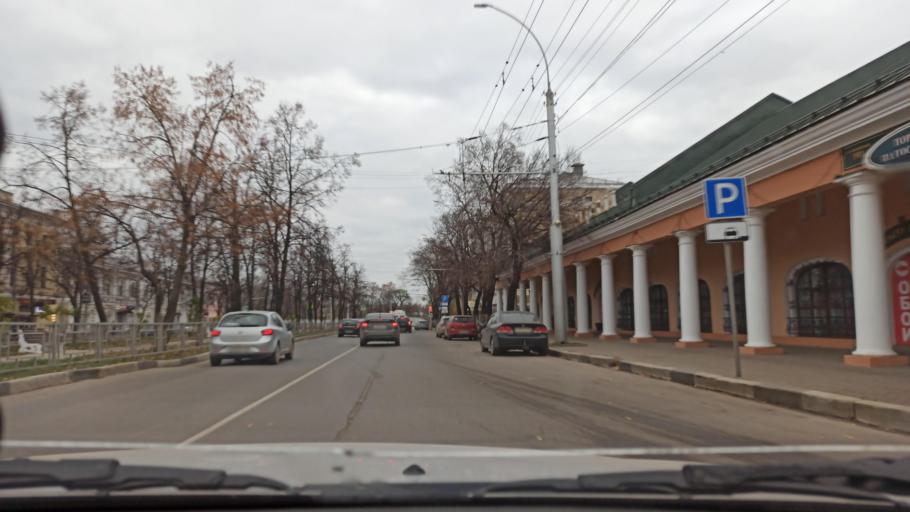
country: RU
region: Vologda
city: Vologda
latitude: 59.2214
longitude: 39.8899
